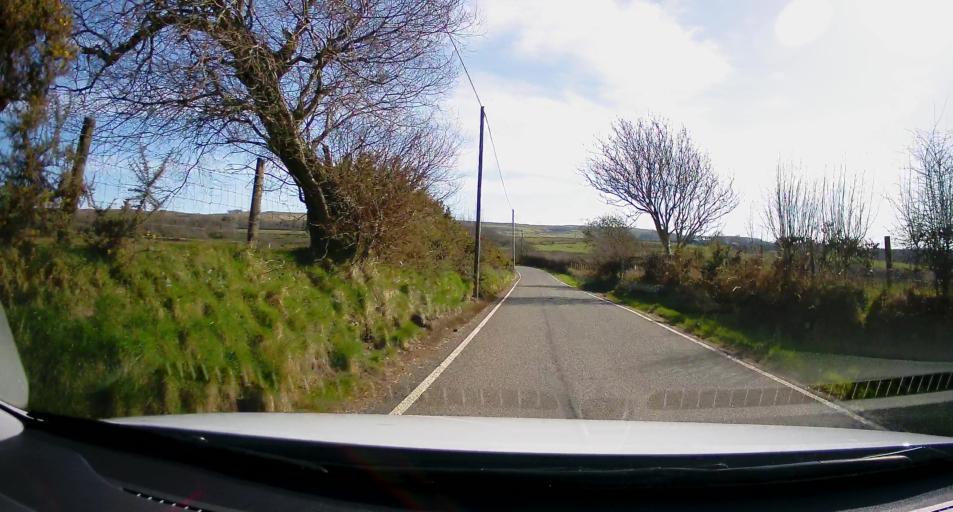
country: GB
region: Wales
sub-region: County of Ceredigion
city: Lledrod
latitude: 52.2938
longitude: -4.0679
